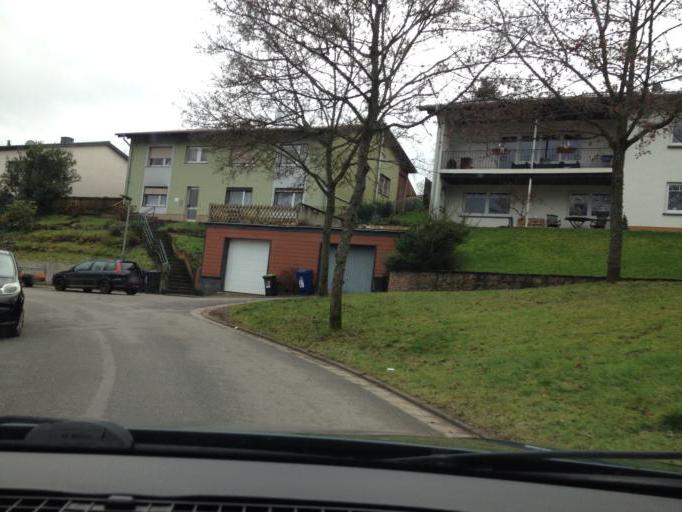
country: DE
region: Saarland
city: Hangard
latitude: 49.3826
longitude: 7.2031
